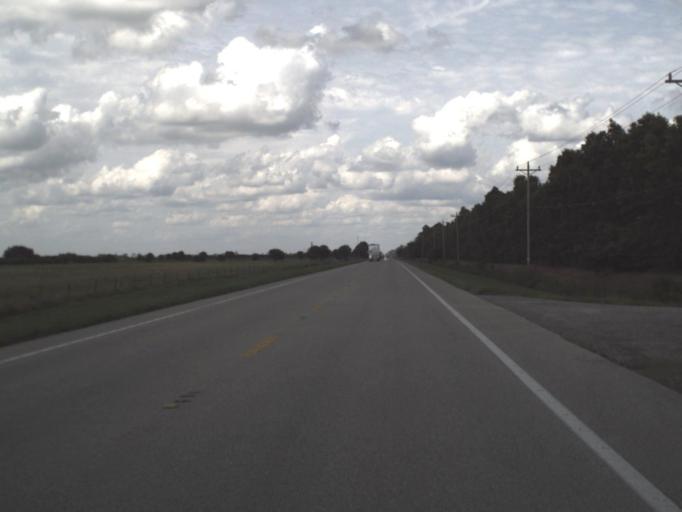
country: US
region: Florida
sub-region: Collier County
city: Immokalee
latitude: 26.5198
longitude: -81.4351
